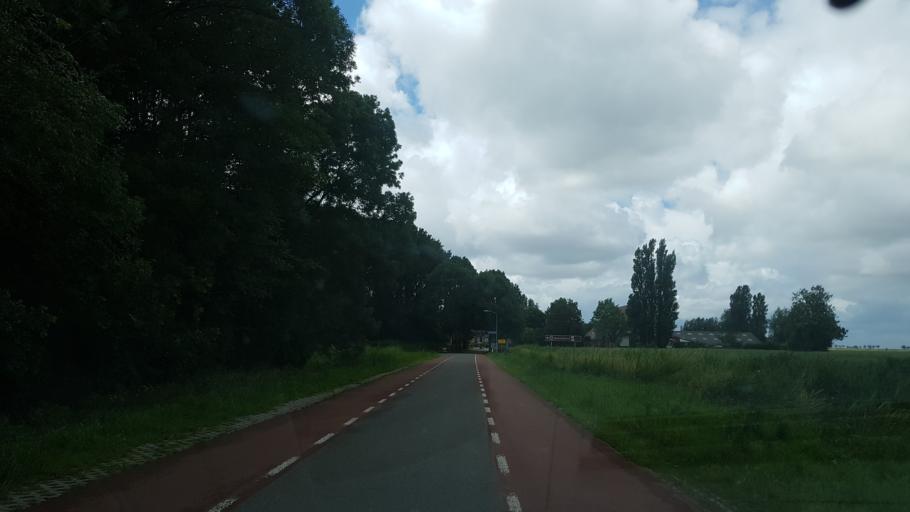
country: NL
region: Groningen
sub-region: Gemeente Winsum
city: Winsum
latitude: 53.3986
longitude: 6.4905
